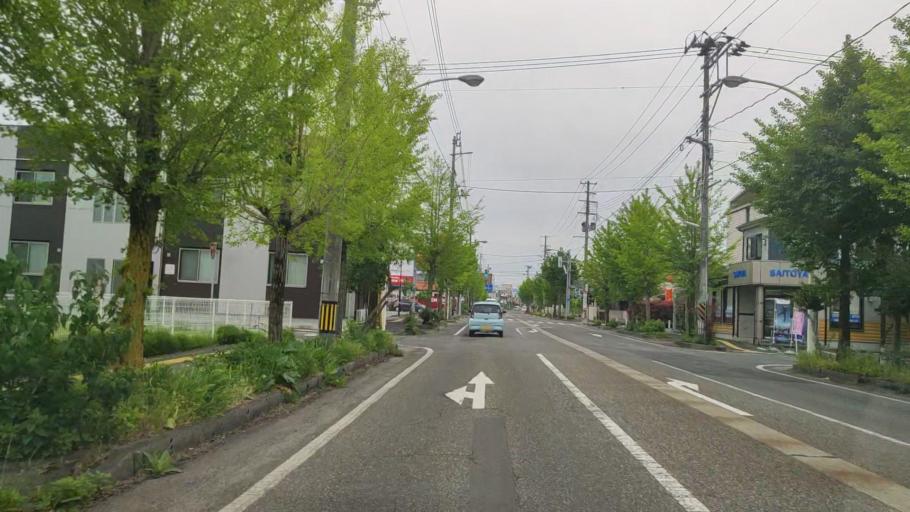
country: JP
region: Niigata
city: Gosen
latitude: 37.7399
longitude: 139.1808
